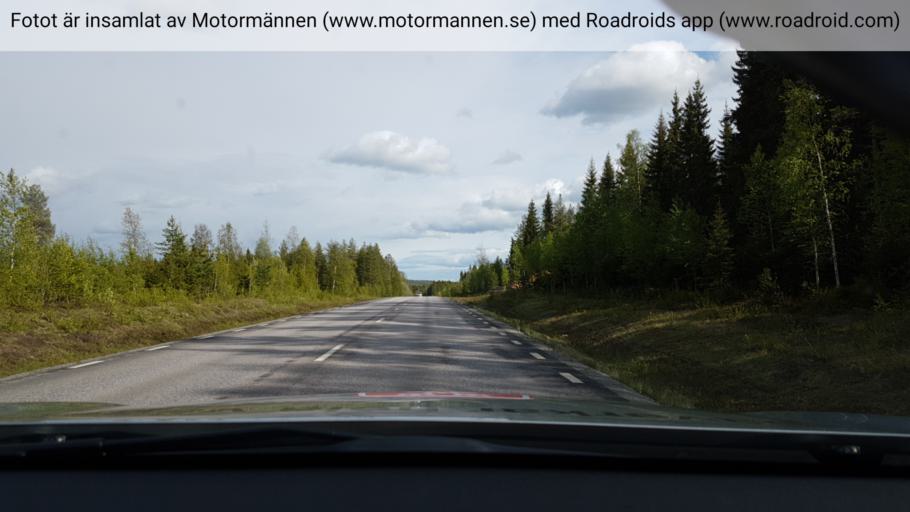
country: SE
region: Vaesterbotten
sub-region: Vannas Kommun
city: Vaennaes
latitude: 63.9079
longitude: 19.6692
